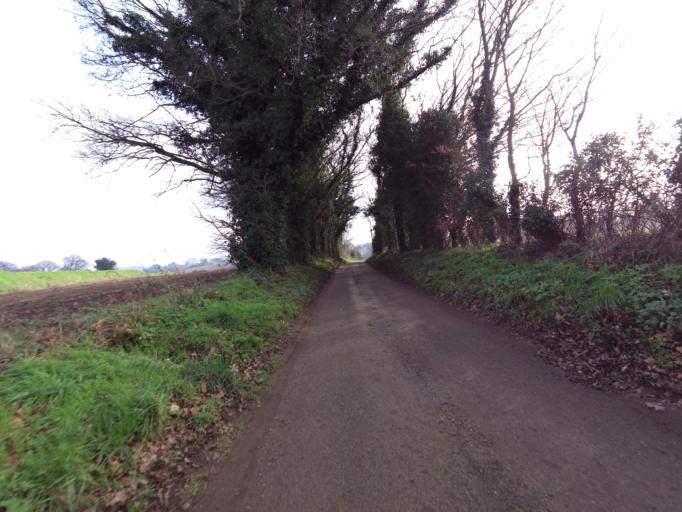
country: GB
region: England
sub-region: Suffolk
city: Woodbridge
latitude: 52.0667
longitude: 1.3054
